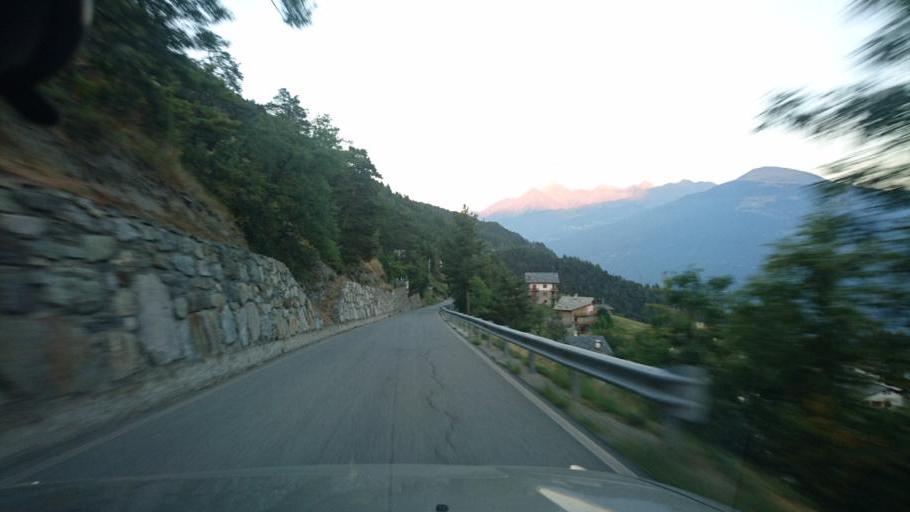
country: IT
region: Aosta Valley
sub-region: Valle d'Aosta
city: Saint-Nicolas
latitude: 45.7179
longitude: 7.1657
